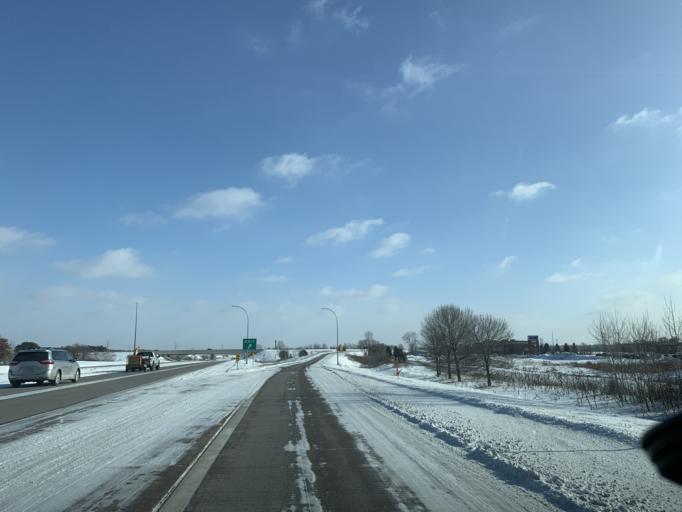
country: US
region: Minnesota
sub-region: Scott County
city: Prior Lake
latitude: 44.7831
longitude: -93.4188
